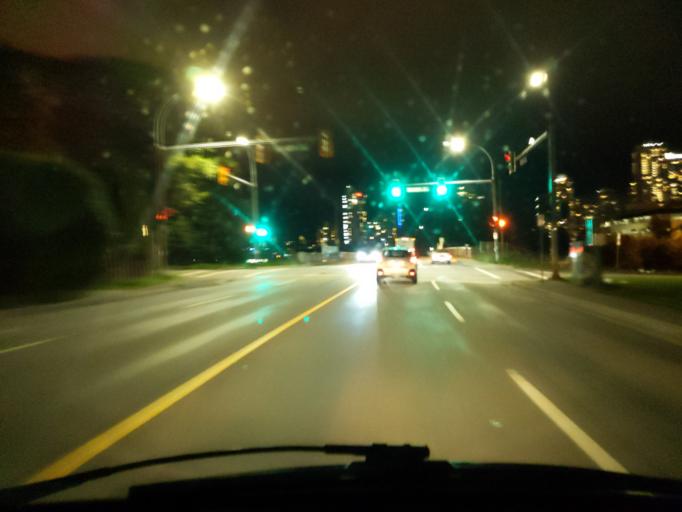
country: CA
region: British Columbia
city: Burnaby
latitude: 49.2569
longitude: -123.0120
